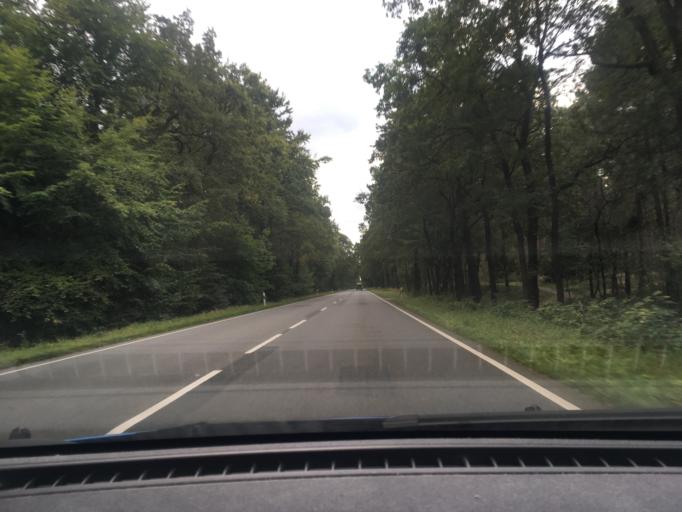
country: DE
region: Lower Saxony
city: Suderburg
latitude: 52.8636
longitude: 10.4928
